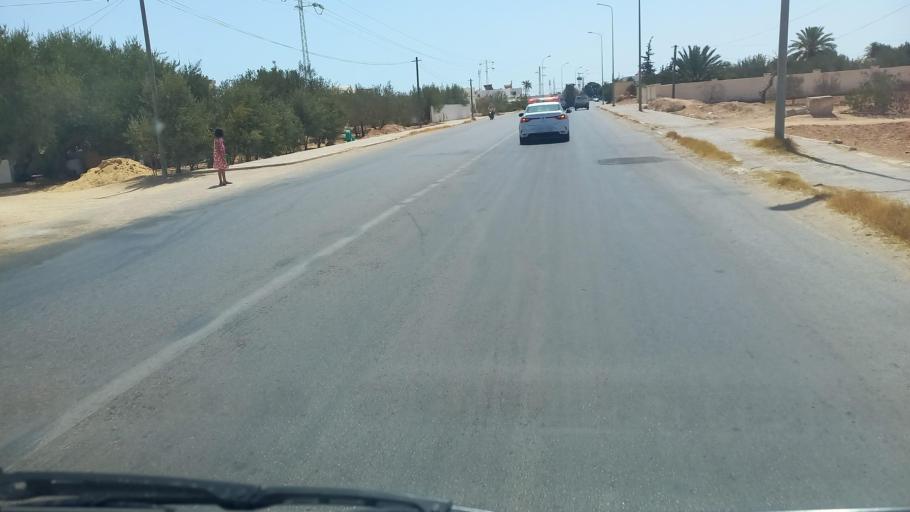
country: TN
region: Madanin
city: Houmt Souk
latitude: 33.7799
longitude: 10.8911
